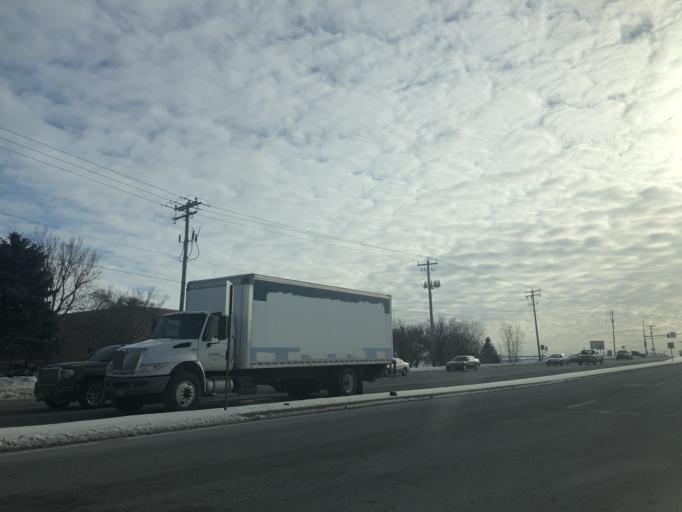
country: US
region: Minnesota
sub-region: Anoka County
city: Circle Pines
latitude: 45.1622
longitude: -93.1634
